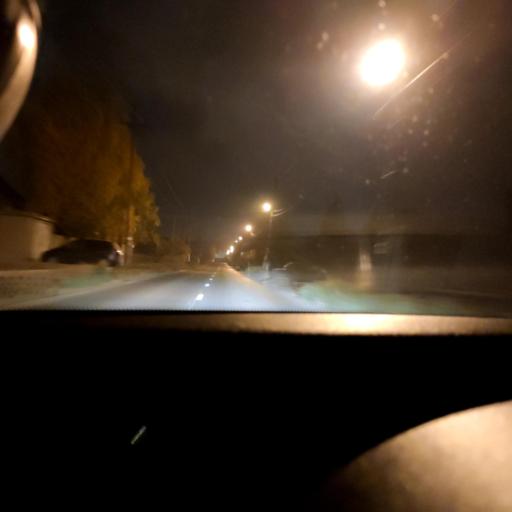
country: RU
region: Samara
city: Petra-Dubrava
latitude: 53.2547
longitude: 50.3178
